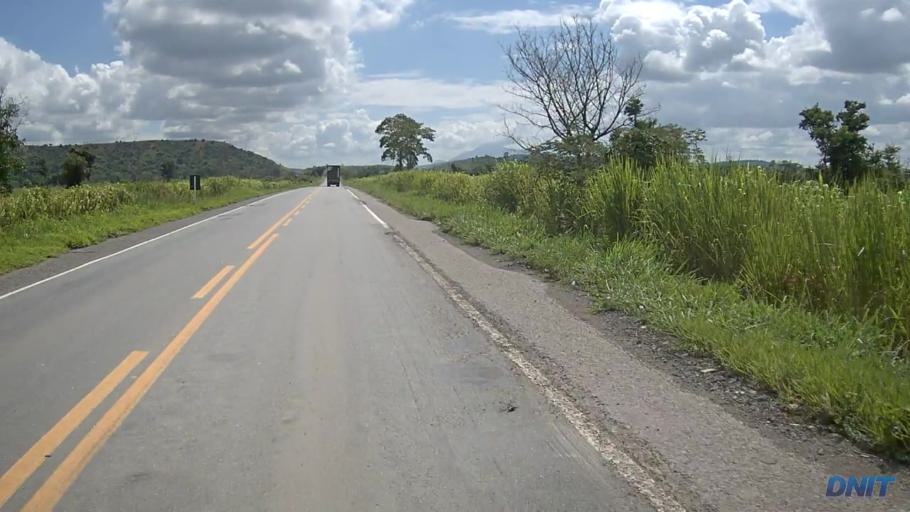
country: BR
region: Minas Gerais
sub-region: Governador Valadares
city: Governador Valadares
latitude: -19.0069
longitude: -42.1329
